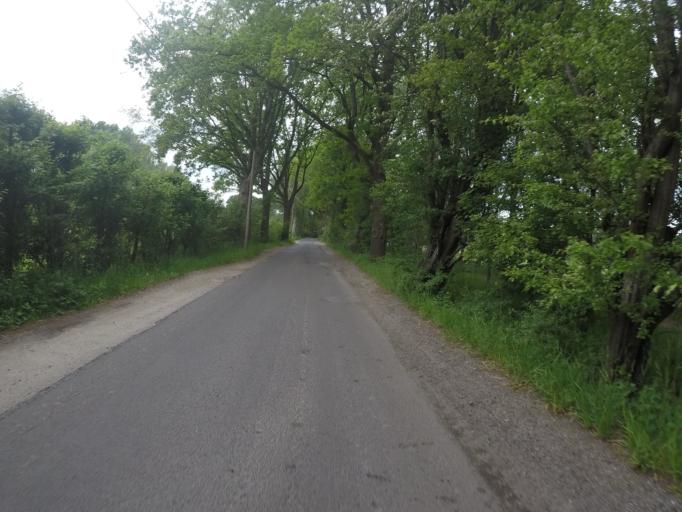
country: DE
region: Schleswig-Holstein
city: Bonningstedt
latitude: 53.6534
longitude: 9.9400
